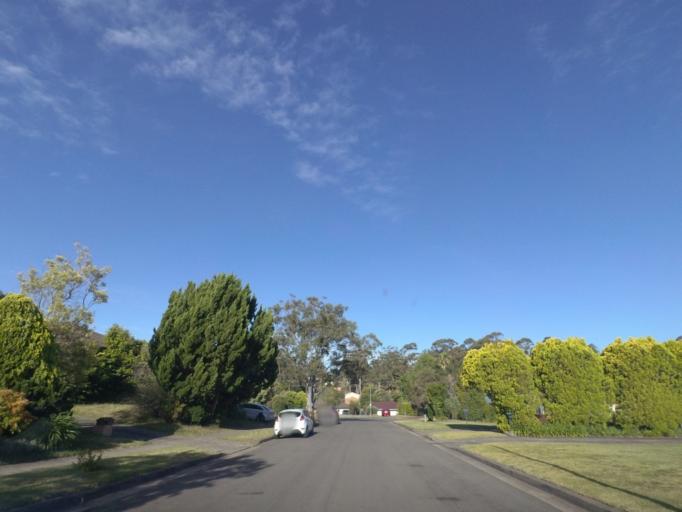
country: AU
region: New South Wales
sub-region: The Hills Shire
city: West Pennant
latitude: -33.7340
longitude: 151.0430
